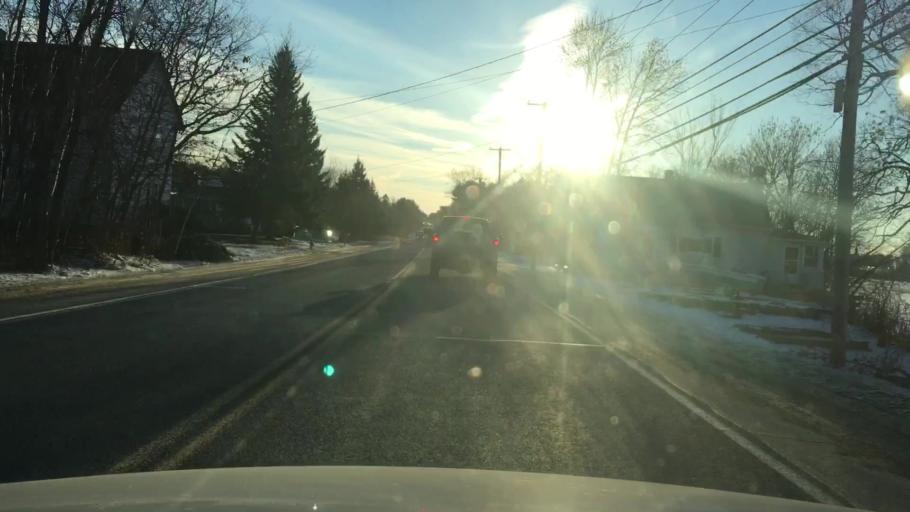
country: US
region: Maine
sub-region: Penobscot County
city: Brewer
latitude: 44.8124
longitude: -68.7336
